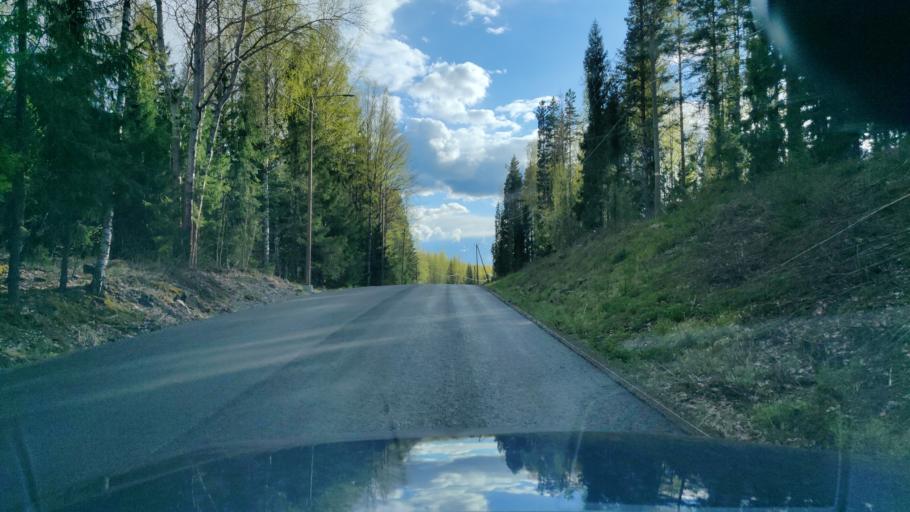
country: FI
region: Uusimaa
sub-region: Helsinki
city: Nurmijaervi
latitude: 60.3601
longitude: 24.7200
